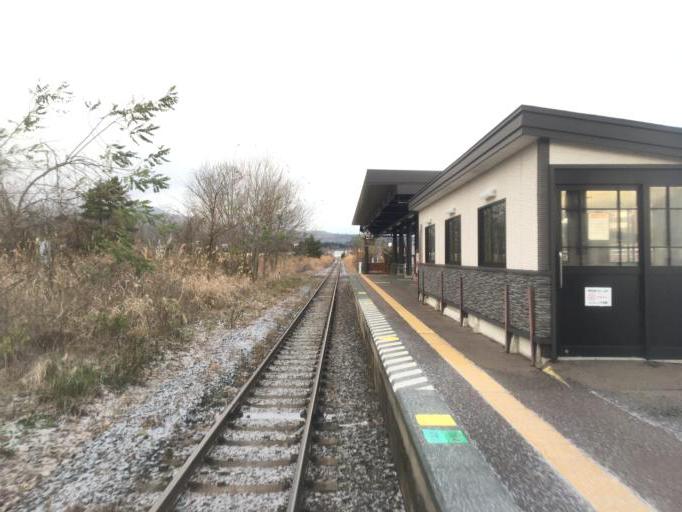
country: JP
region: Aomori
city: Mutsu
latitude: 41.2829
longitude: 141.1900
